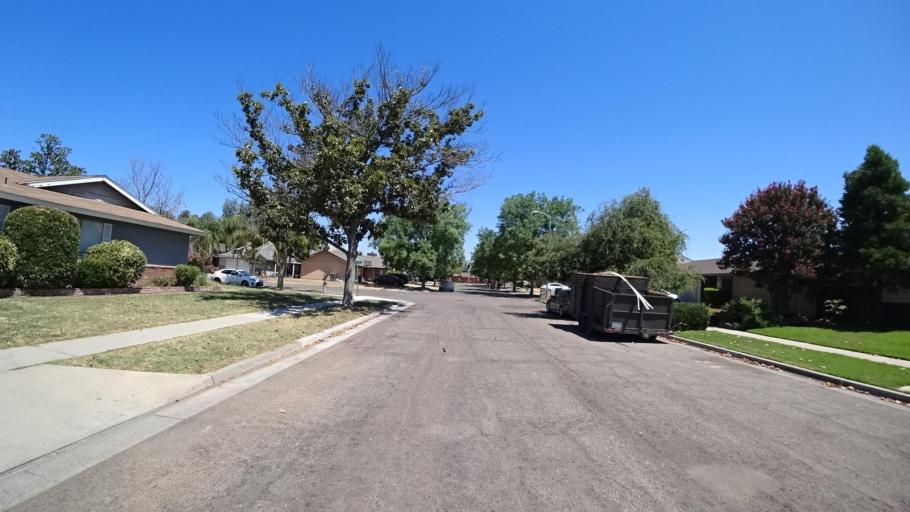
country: US
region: California
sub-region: Fresno County
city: Sunnyside
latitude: 36.7683
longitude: -119.7333
